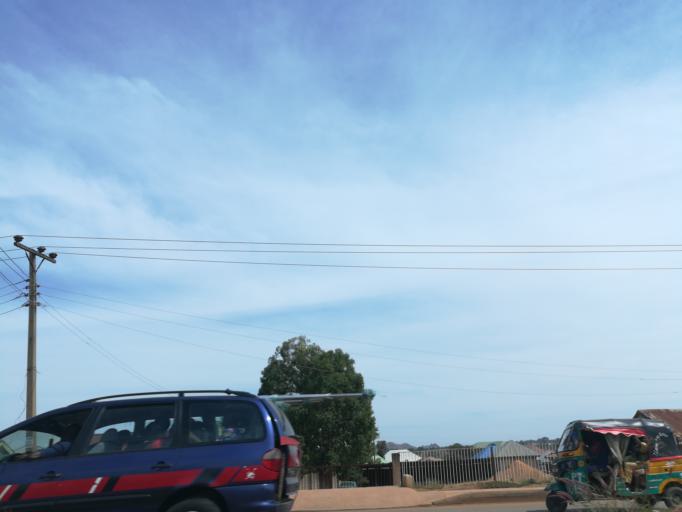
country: NG
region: Plateau
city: Bukuru
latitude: 9.7713
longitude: 8.8604
